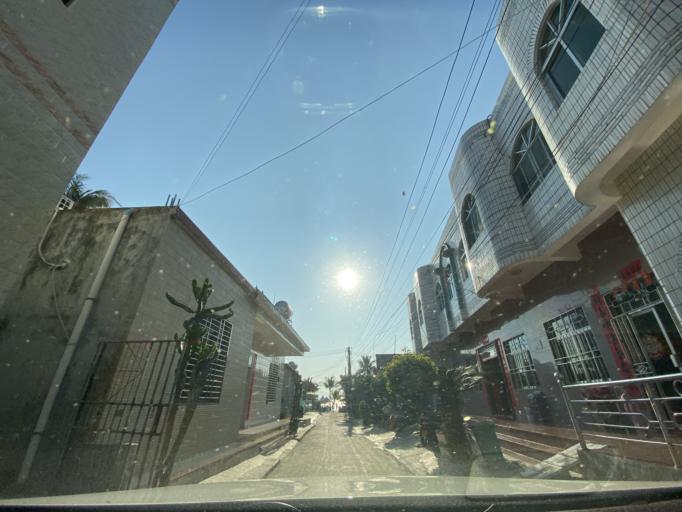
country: CN
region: Hainan
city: Yingzhou
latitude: 18.3892
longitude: 109.8181
